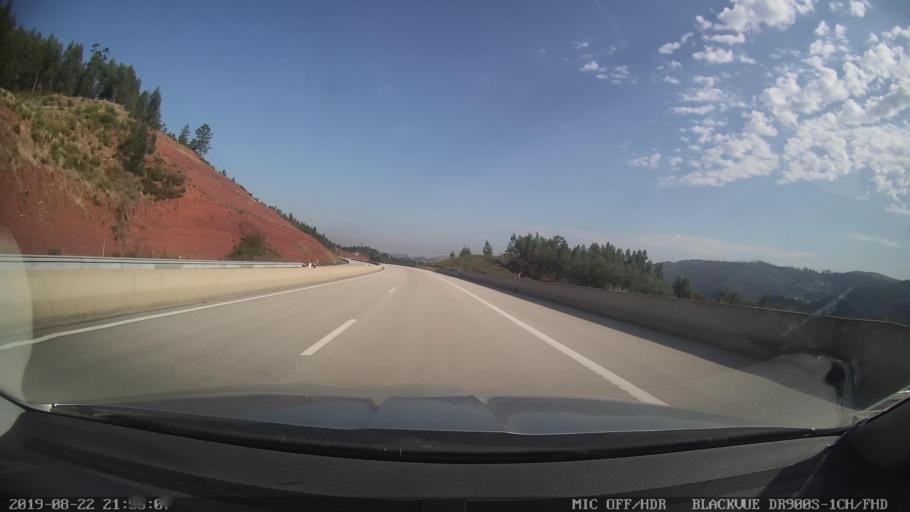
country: PT
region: Coimbra
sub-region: Coimbra
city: Coimbra
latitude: 40.1476
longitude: -8.3831
